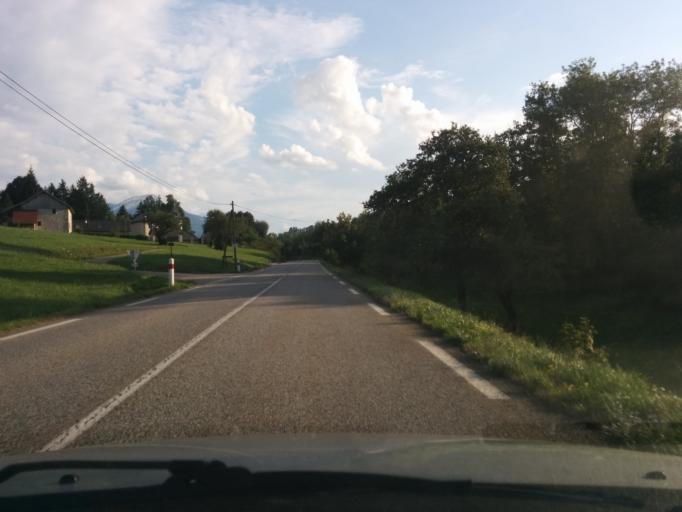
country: FR
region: Rhone-Alpes
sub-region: Departement de la Savoie
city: Les Echelles
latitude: 45.4572
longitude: 5.7363
